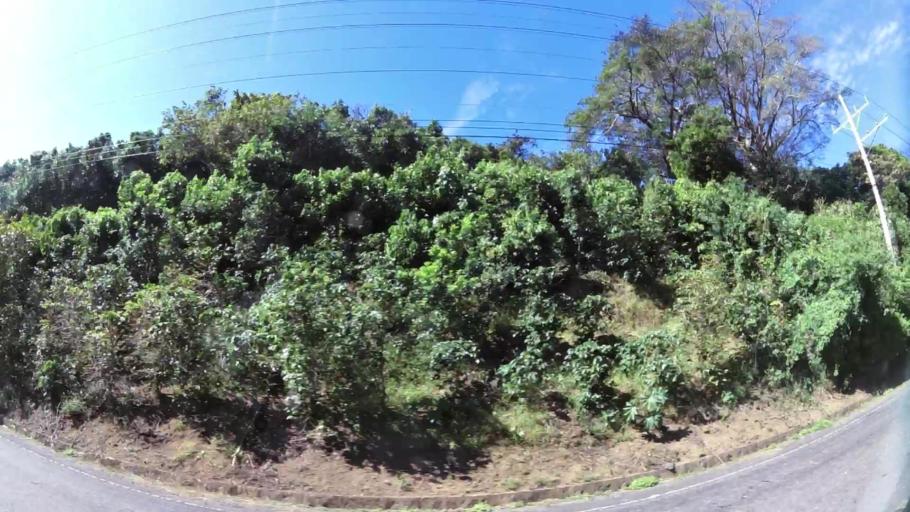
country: SV
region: Sonsonate
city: Juayua
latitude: 13.8546
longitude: -89.7870
